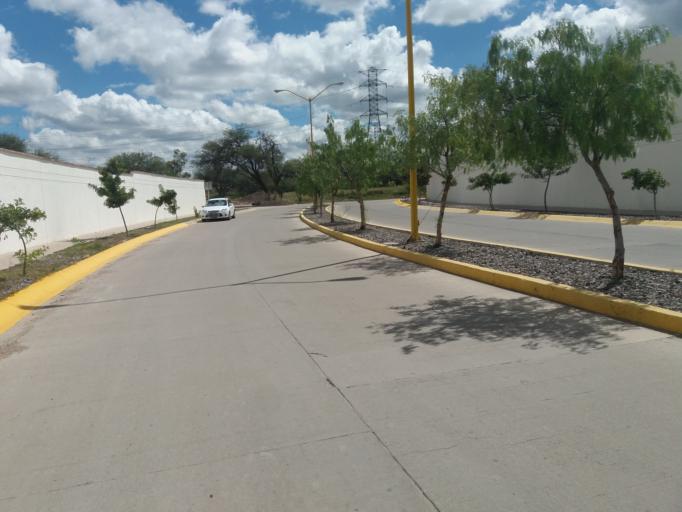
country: MX
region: Aguascalientes
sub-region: Aguascalientes
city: San Sebastian [Fraccionamiento]
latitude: 21.8196
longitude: -102.2724
